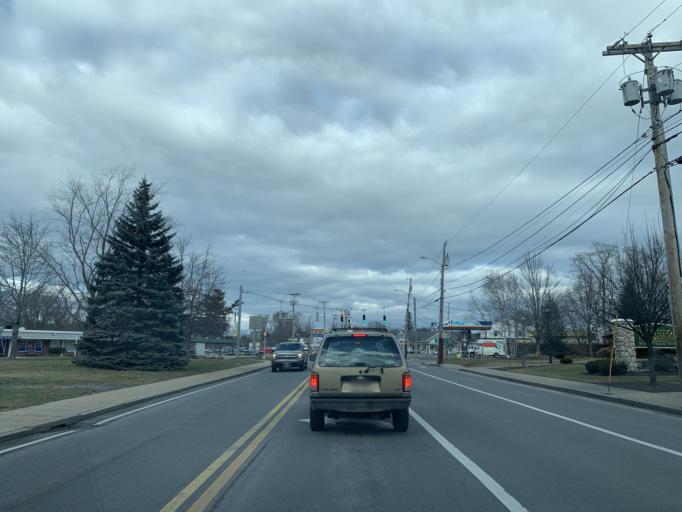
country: US
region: Massachusetts
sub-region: Essex County
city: Salisbury
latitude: 42.8403
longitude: -70.8607
